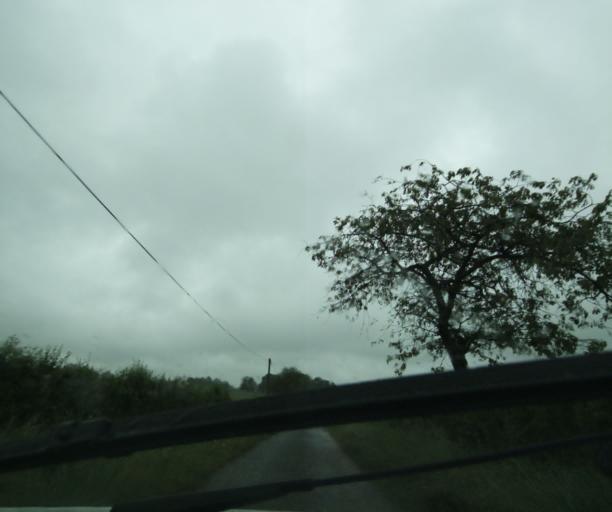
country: FR
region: Bourgogne
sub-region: Departement de Saone-et-Loire
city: Ciry-le-Noble
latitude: 46.5623
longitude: 4.3216
